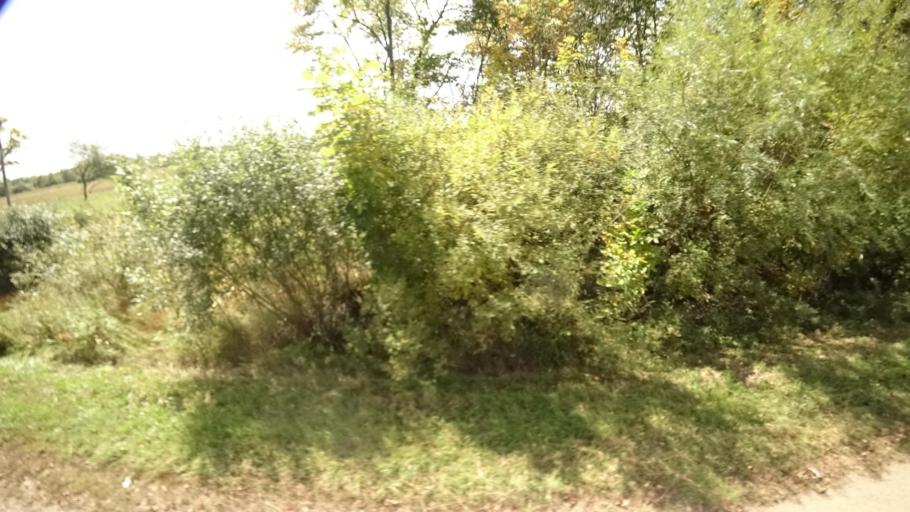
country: RU
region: Primorskiy
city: Yakovlevka
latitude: 44.6371
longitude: 133.5971
